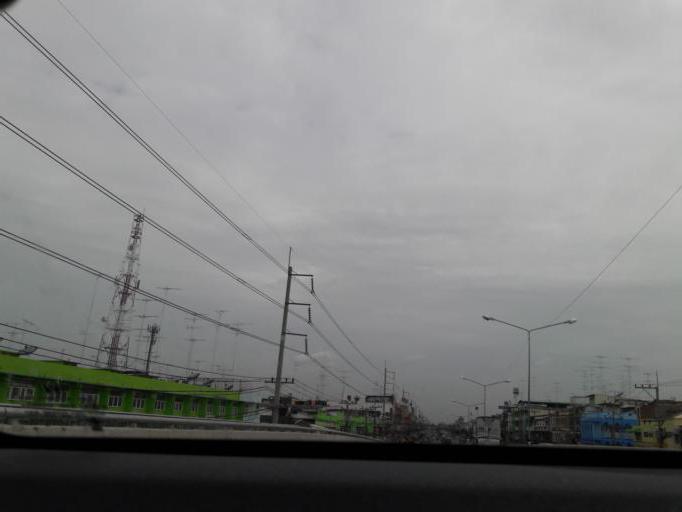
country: TH
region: Ratchaburi
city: Damnoen Saduak
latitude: 13.5268
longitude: 99.9692
